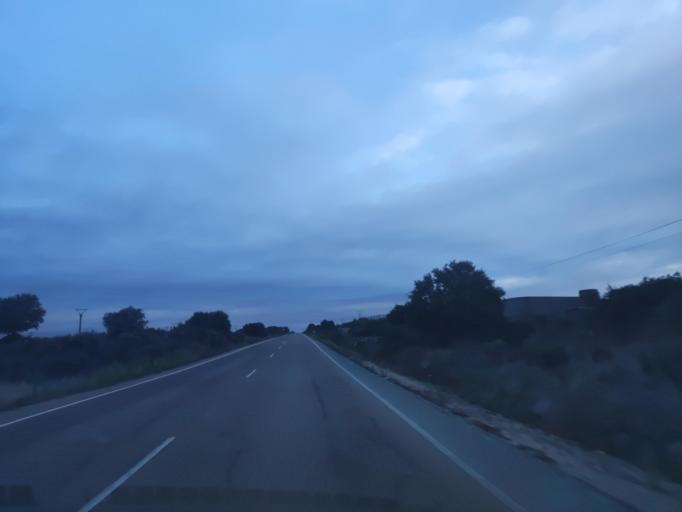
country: ES
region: Castille and Leon
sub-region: Provincia de Salamanca
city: Lumbrales
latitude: 40.8971
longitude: -6.7157
